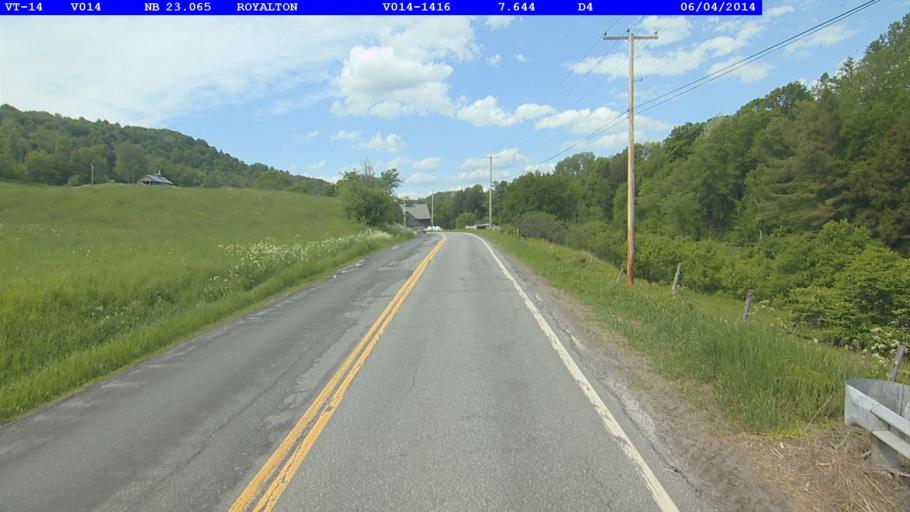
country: US
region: Vermont
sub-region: Orange County
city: Randolph
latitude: 43.8454
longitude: -72.5869
